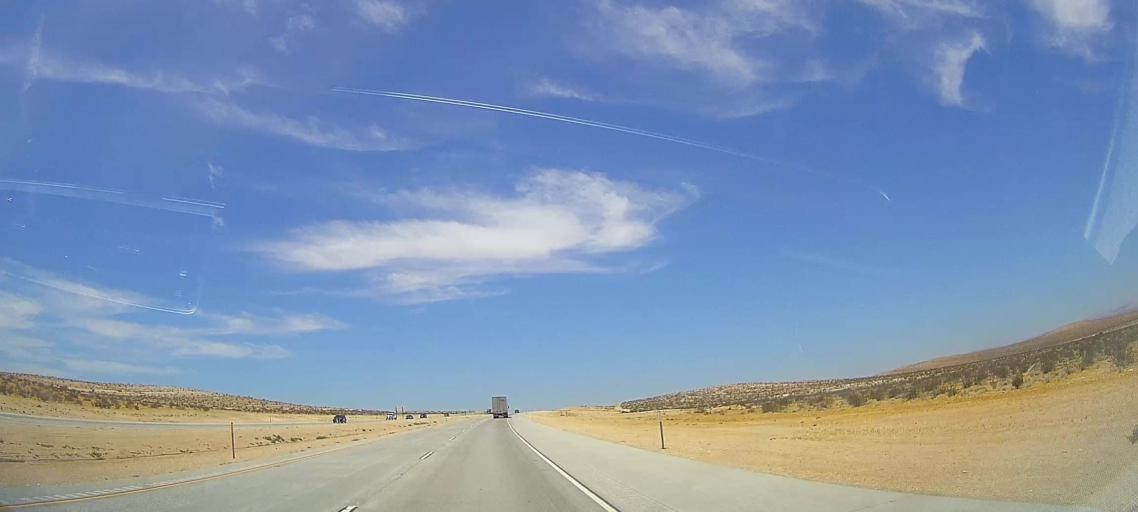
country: US
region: California
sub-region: San Bernardino County
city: Lenwood
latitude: 34.9140
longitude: -117.2279
